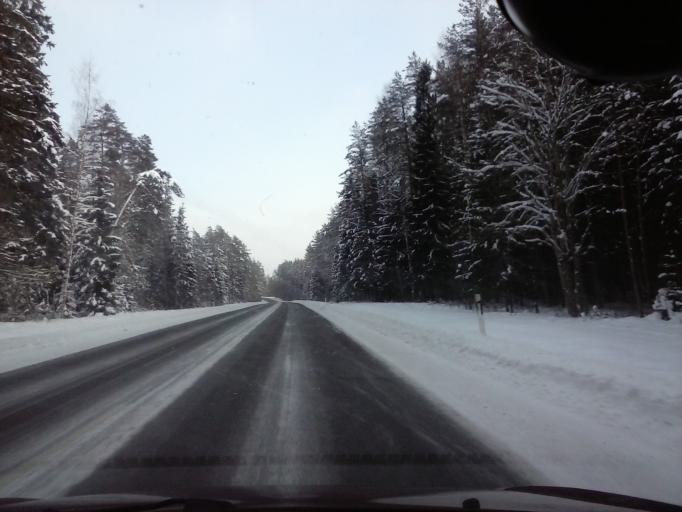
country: EE
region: Viljandimaa
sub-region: Moisakuela linn
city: Moisakula
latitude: 58.2472
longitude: 25.1554
